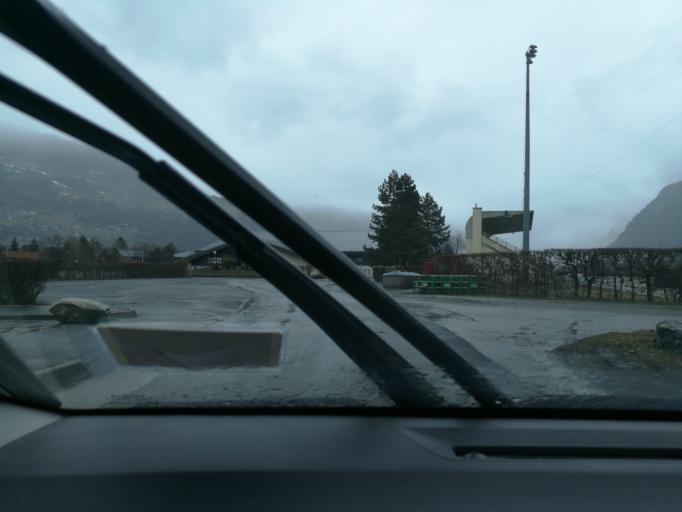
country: FR
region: Rhone-Alpes
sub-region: Departement de la Haute-Savoie
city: Sallanches
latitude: 45.9323
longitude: 6.6442
